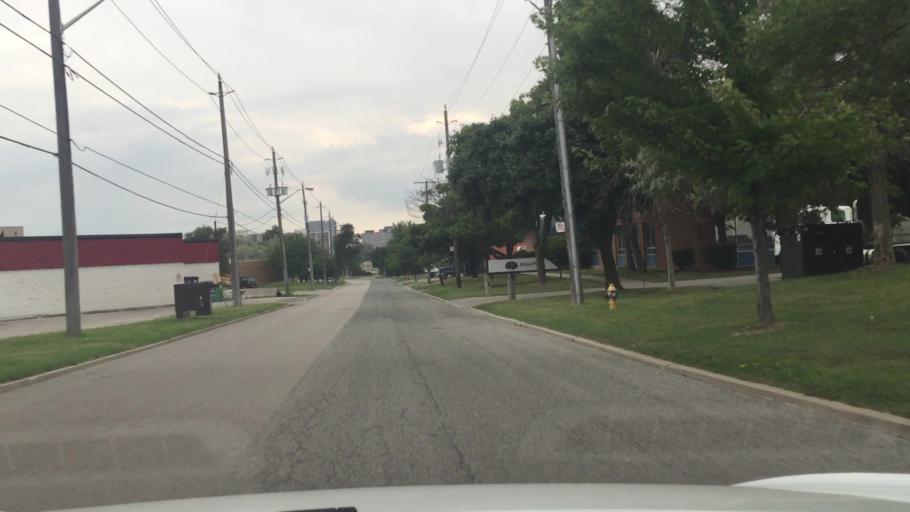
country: CA
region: Ontario
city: Scarborough
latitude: 43.7159
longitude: -79.3093
